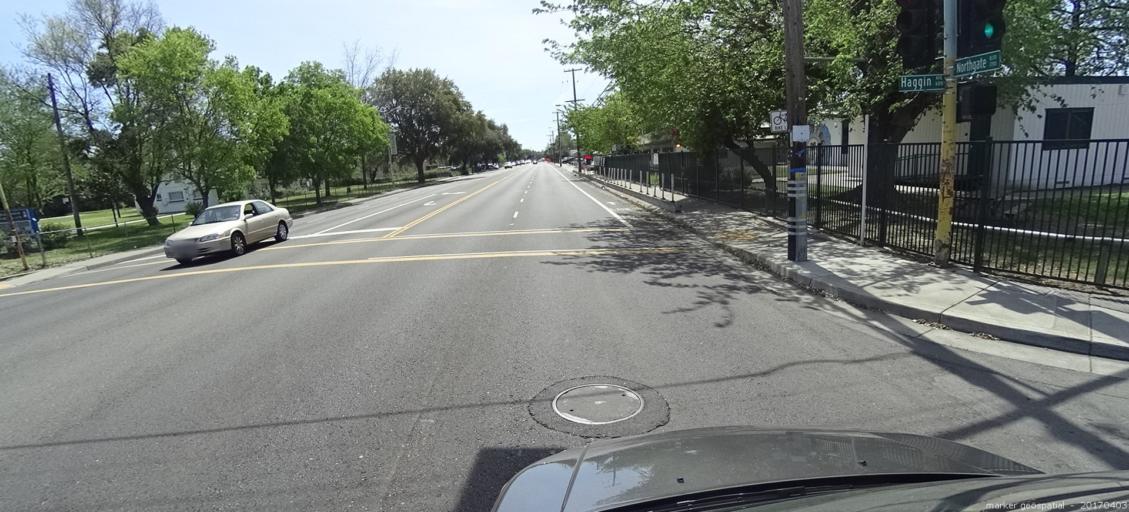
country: US
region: California
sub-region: Sacramento County
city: Sacramento
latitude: 38.6159
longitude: -121.4756
